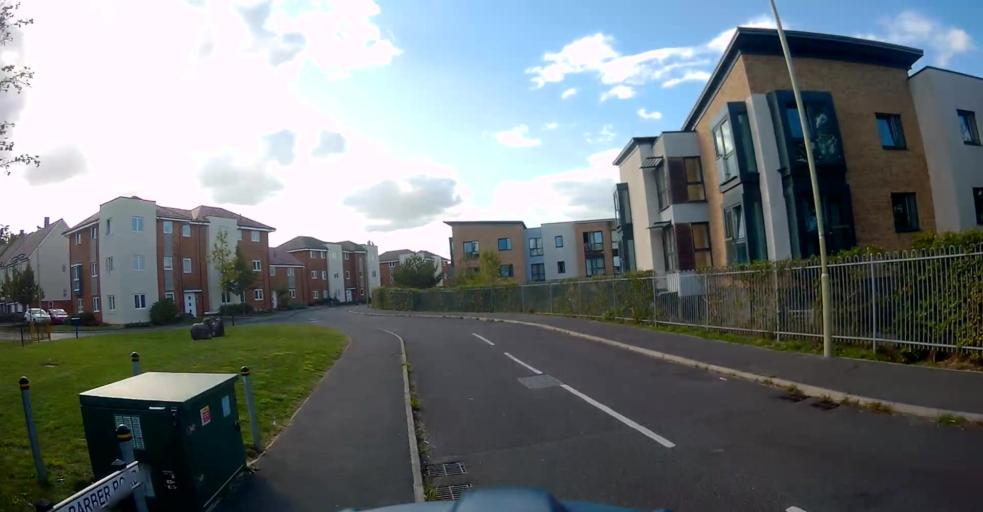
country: GB
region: England
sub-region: Hampshire
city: Basingstoke
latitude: 51.2435
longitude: -1.1178
